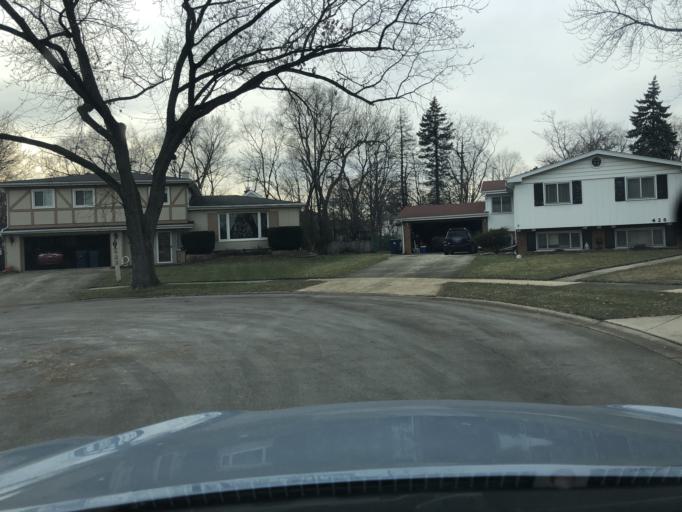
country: US
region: Illinois
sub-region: DuPage County
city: Addison
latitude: 41.9347
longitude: -88.0099
